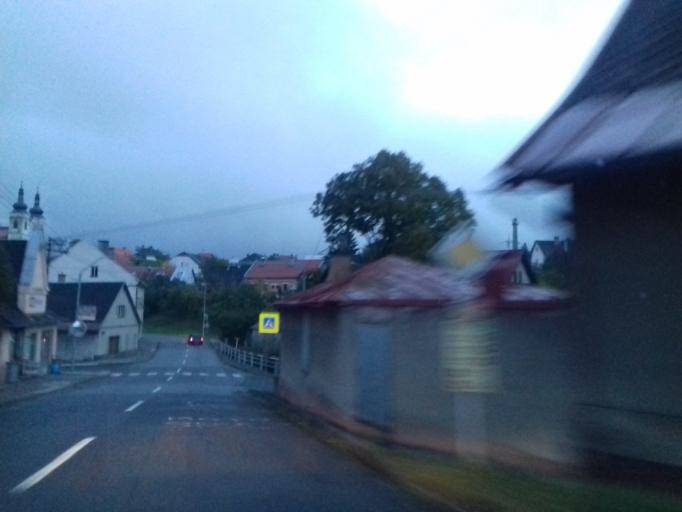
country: CZ
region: Pardubicky
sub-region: Okres Svitavy
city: Bystre
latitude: 49.6311
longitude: 16.3425
